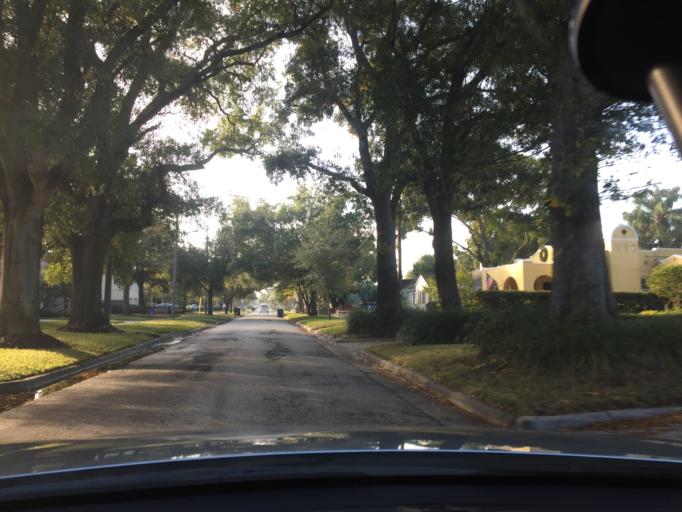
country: US
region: Florida
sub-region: Hillsborough County
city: Tampa
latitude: 27.9441
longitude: -82.4974
